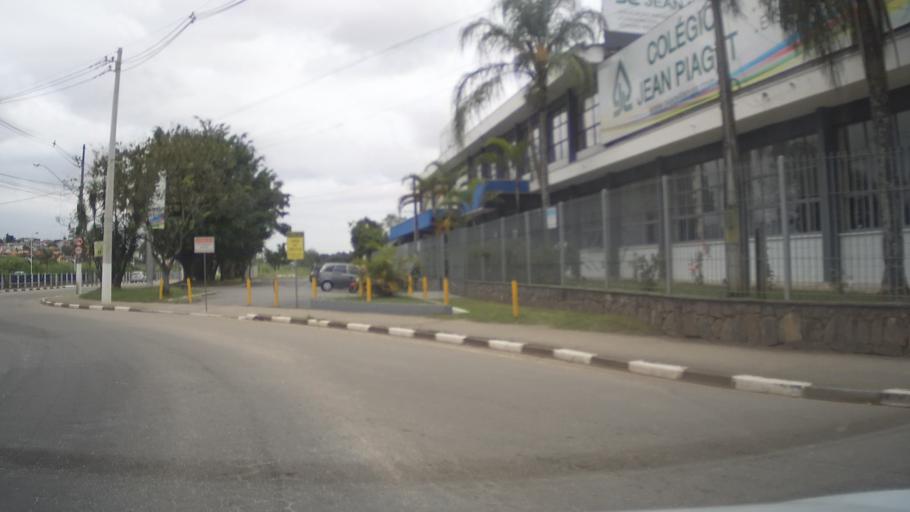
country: BR
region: Sao Paulo
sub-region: Aruja
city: Aruja
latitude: -23.3968
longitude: -46.3342
